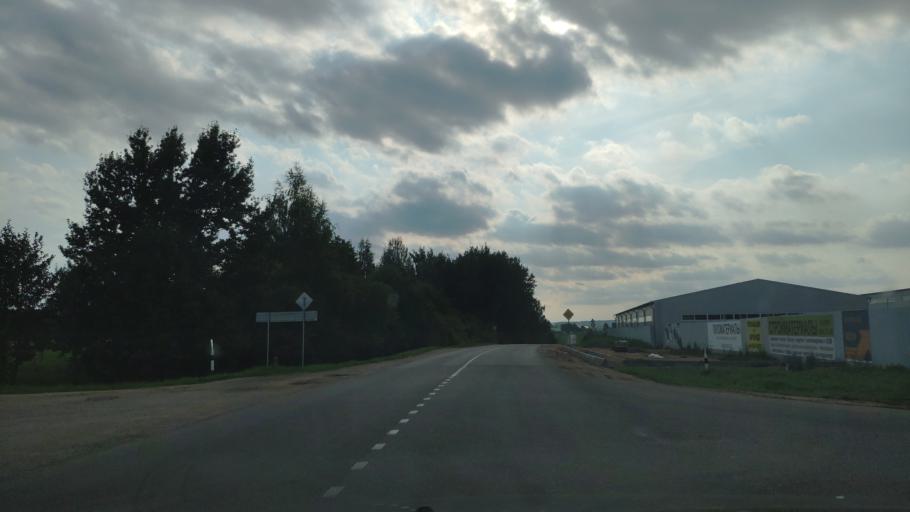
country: BY
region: Minsk
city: Azyartso
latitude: 53.8384
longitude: 27.3737
